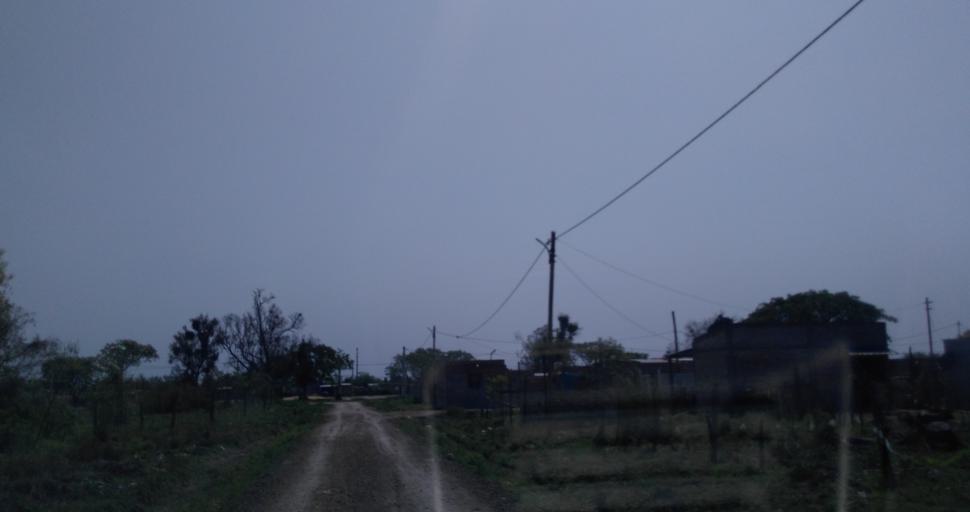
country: AR
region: Chaco
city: Fontana
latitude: -27.4183
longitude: -59.0182
